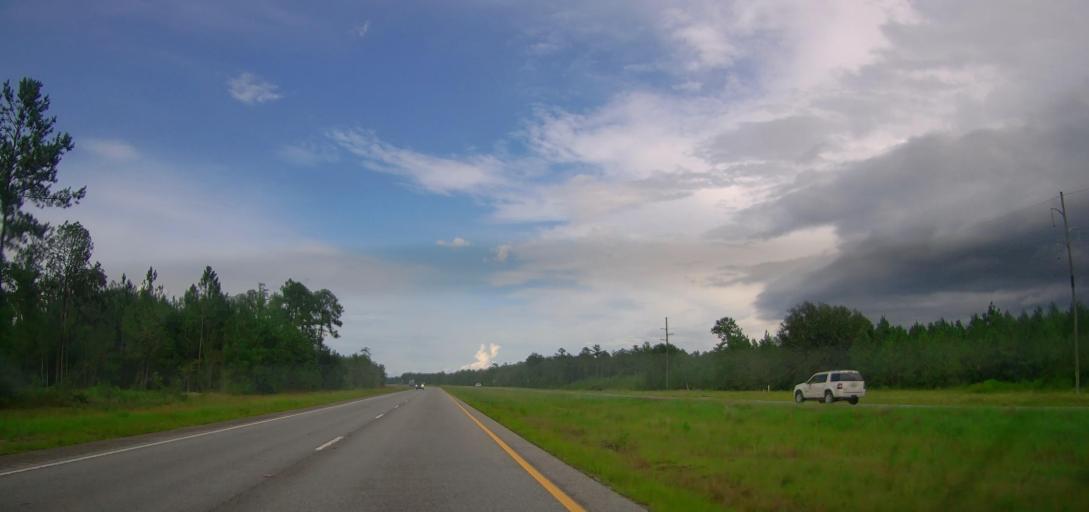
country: US
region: Georgia
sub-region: Pierce County
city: Blackshear
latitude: 31.4467
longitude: -82.0692
